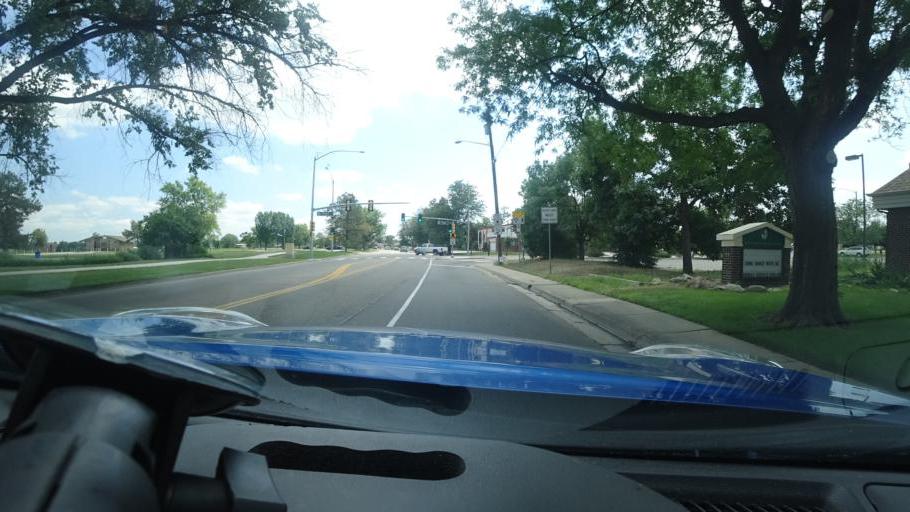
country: US
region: Colorado
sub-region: Adams County
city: Aurora
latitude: 39.7226
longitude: -104.8479
